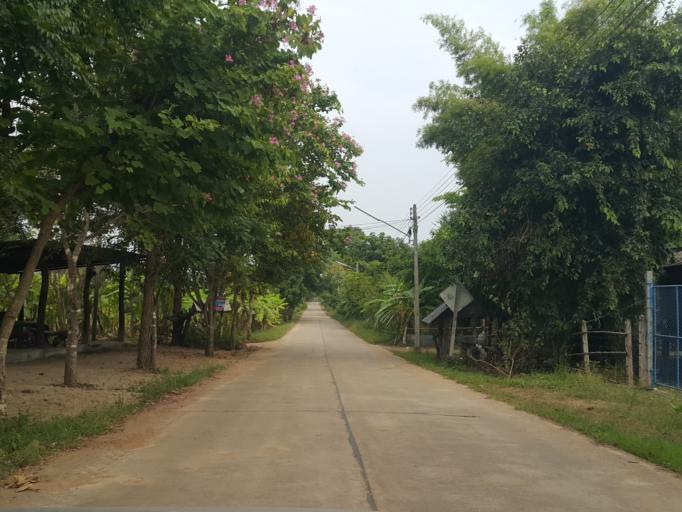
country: TH
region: Mae Hong Son
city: Wiang Nuea
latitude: 19.3700
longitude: 98.4488
